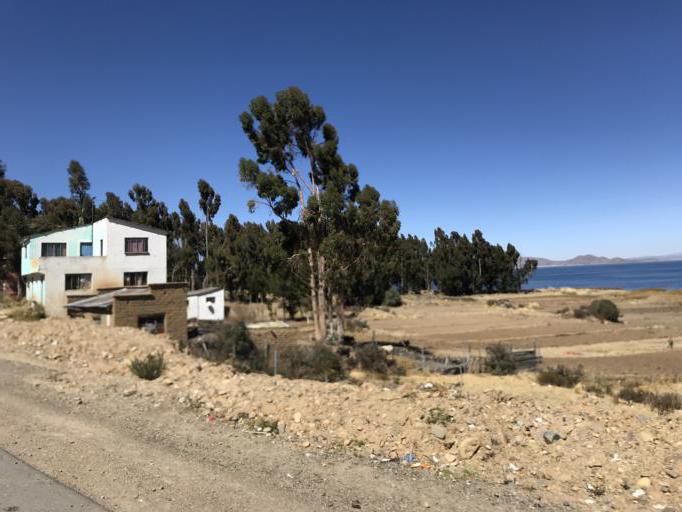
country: BO
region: La Paz
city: Huatajata
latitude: -16.2156
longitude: -68.6655
